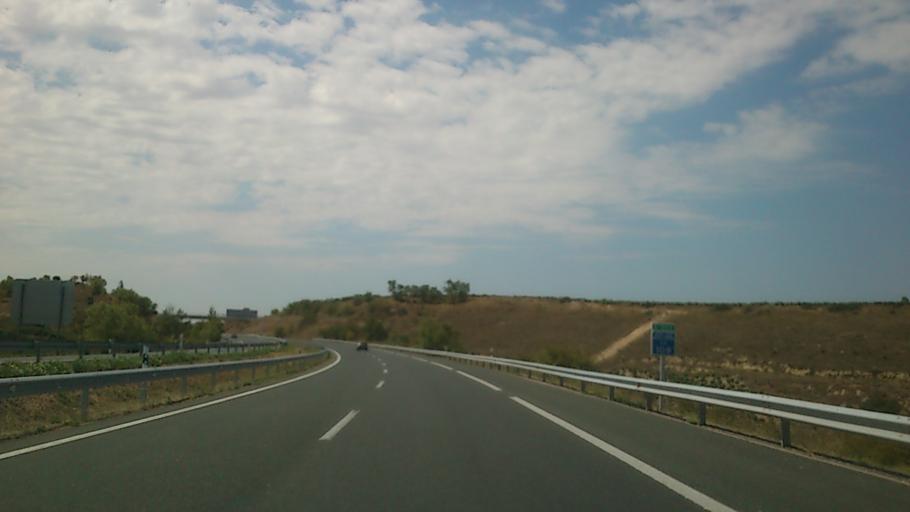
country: ES
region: La Rioja
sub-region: Provincia de La Rioja
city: Cenicero
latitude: 42.4775
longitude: -2.6537
